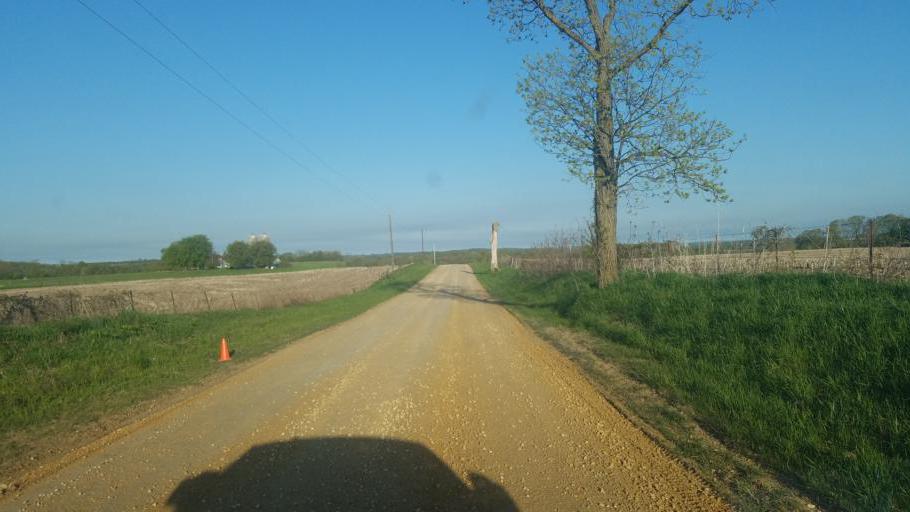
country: US
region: Wisconsin
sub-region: Vernon County
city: Hillsboro
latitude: 43.5673
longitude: -90.5261
